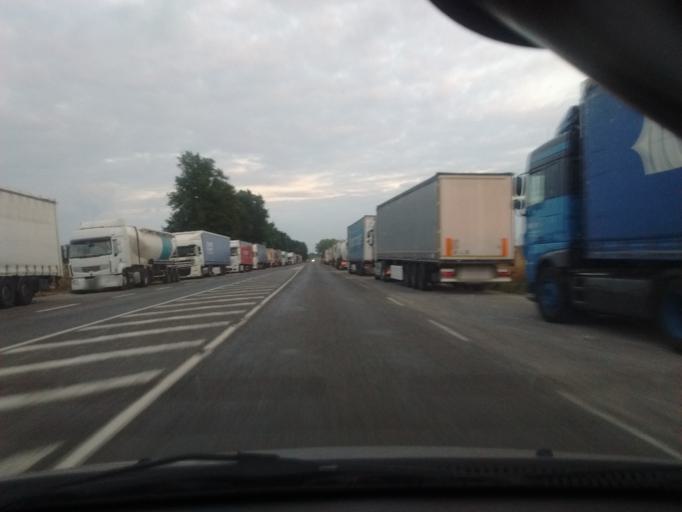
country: FR
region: Ile-de-France
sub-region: Departement de Seine-et-Marne
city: Pringy
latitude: 48.5097
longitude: 2.5713
